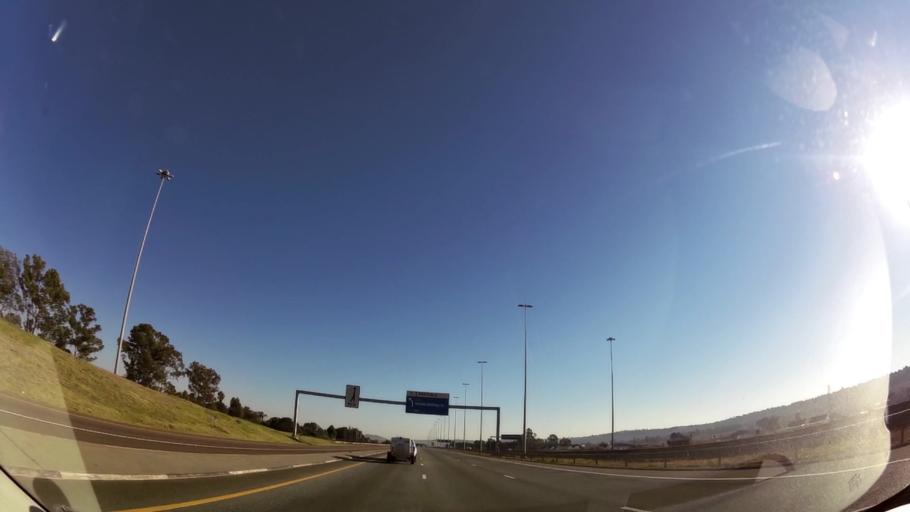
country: ZA
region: Gauteng
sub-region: City of Tshwane Metropolitan Municipality
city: Centurion
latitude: -25.8274
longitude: 28.2424
